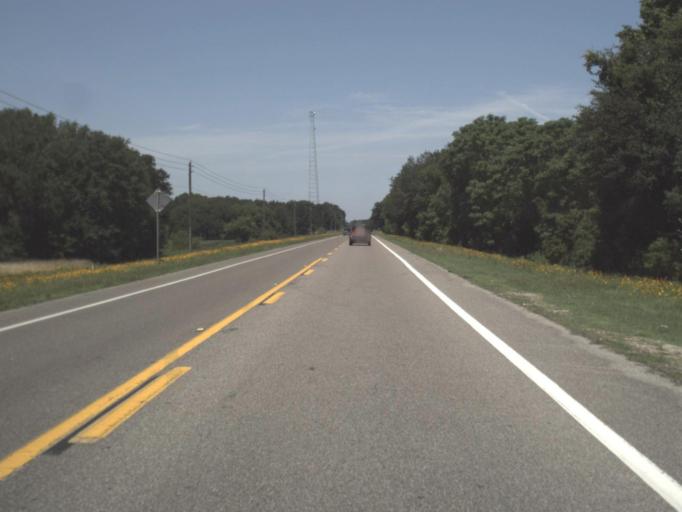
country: US
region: Florida
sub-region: Suwannee County
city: Live Oak
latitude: 30.2717
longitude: -82.9298
